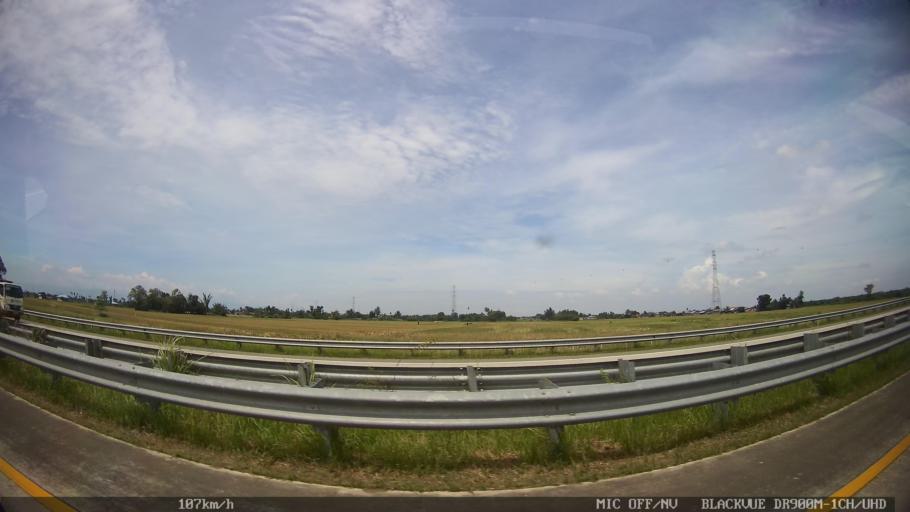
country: ID
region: North Sumatra
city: Percut
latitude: 3.5764
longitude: 98.8468
